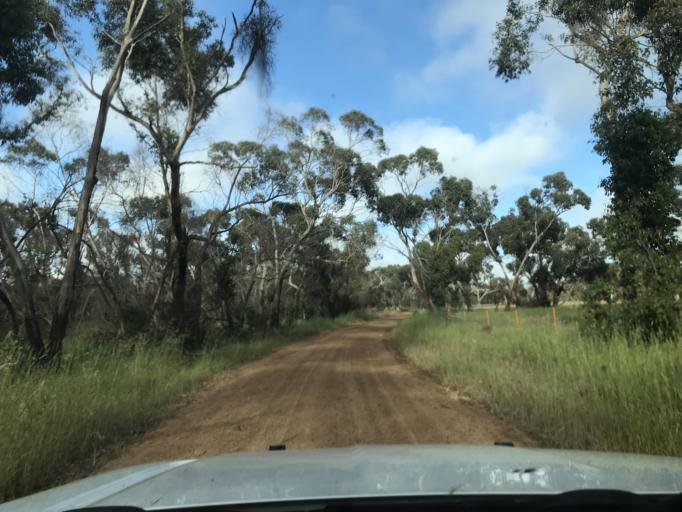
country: AU
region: South Australia
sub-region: Wattle Range
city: Penola
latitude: -37.1813
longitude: 141.1773
